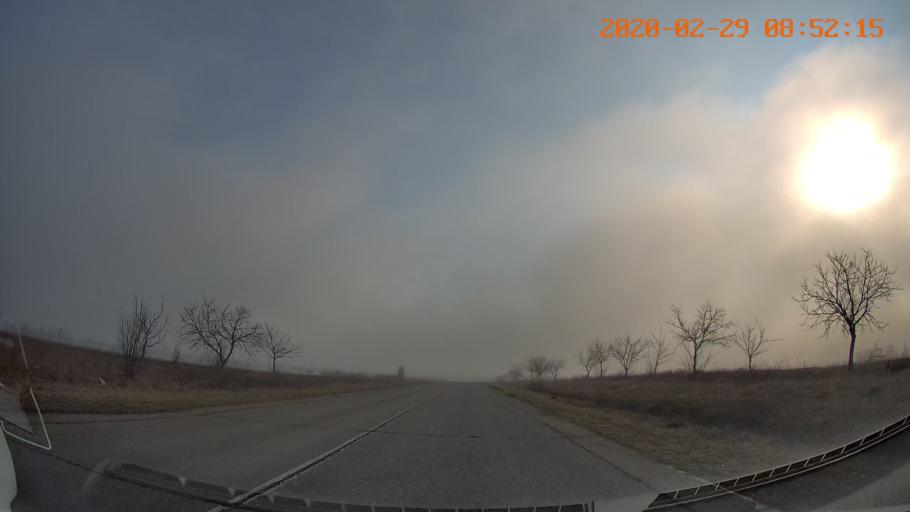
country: MD
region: Anenii Noi
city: Varnita
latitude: 46.9232
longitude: 29.5345
